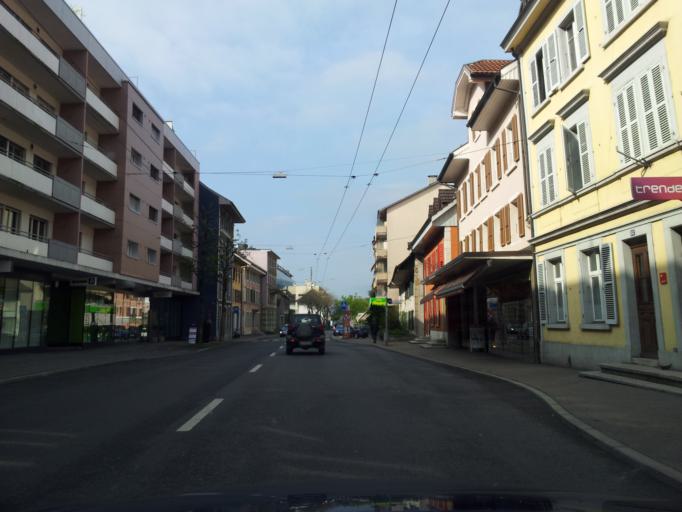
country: CH
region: Bern
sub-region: Biel/Bienne District
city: Biel/Bienne
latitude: 47.1518
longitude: 7.2656
